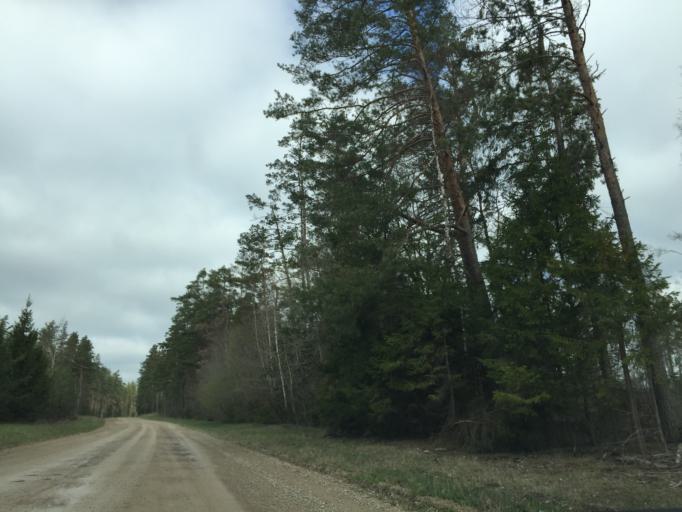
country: EE
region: Valgamaa
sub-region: Valga linn
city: Valga
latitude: 57.6252
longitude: 26.2357
